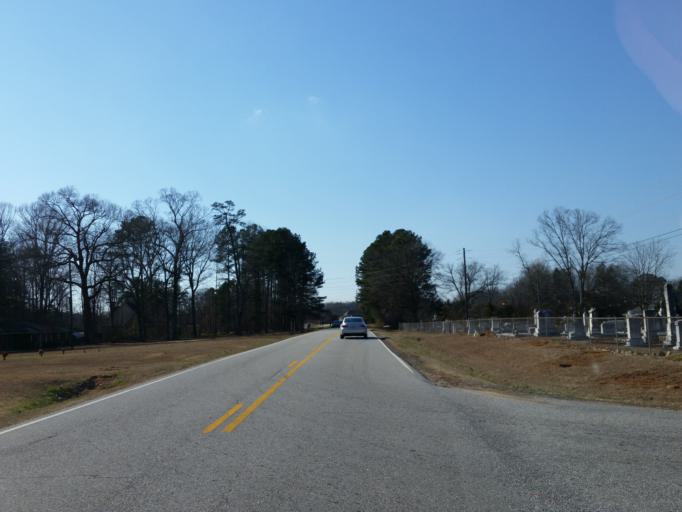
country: US
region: Georgia
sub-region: Henry County
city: Hampton
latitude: 33.4415
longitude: -84.2505
